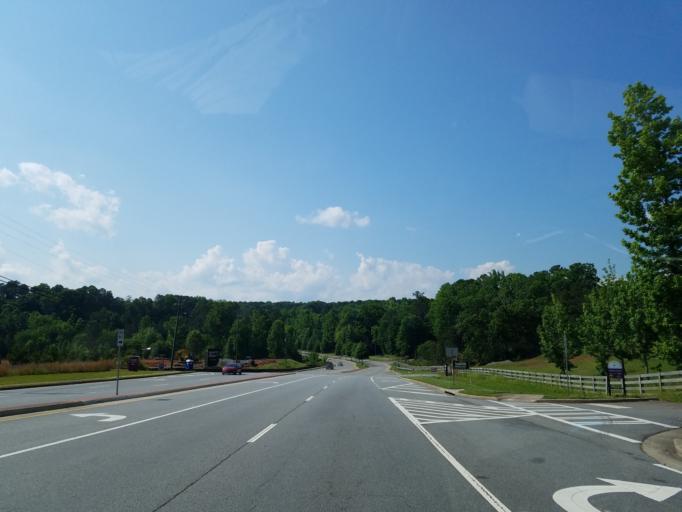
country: US
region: Georgia
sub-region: Cherokee County
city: Holly Springs
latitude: 34.1487
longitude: -84.5187
